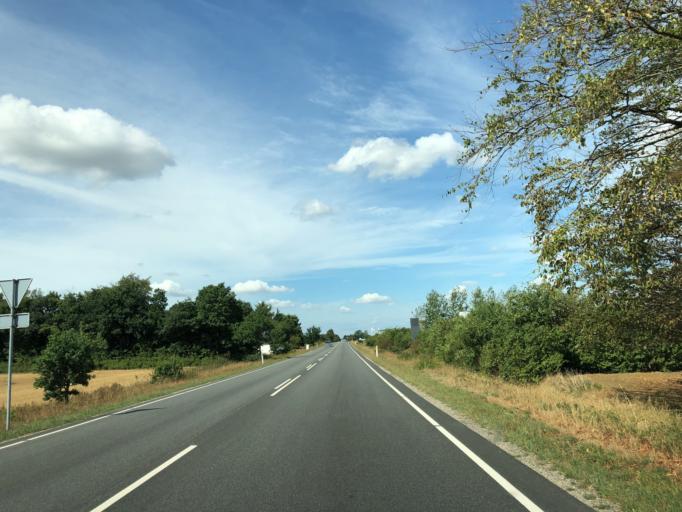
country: DK
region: Central Jutland
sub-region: Ikast-Brande Kommune
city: Bording Kirkeby
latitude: 56.1410
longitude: 9.2698
